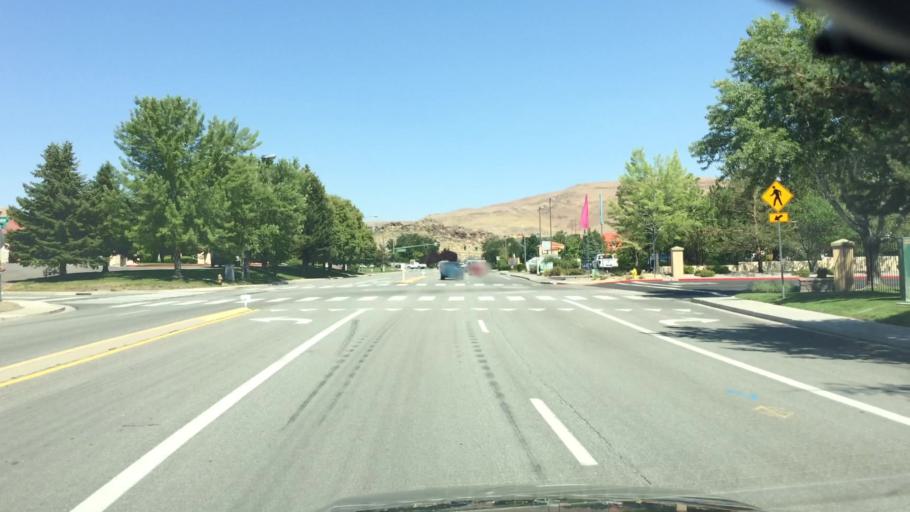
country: US
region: Nevada
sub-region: Washoe County
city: Sparks
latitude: 39.5583
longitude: -119.7084
